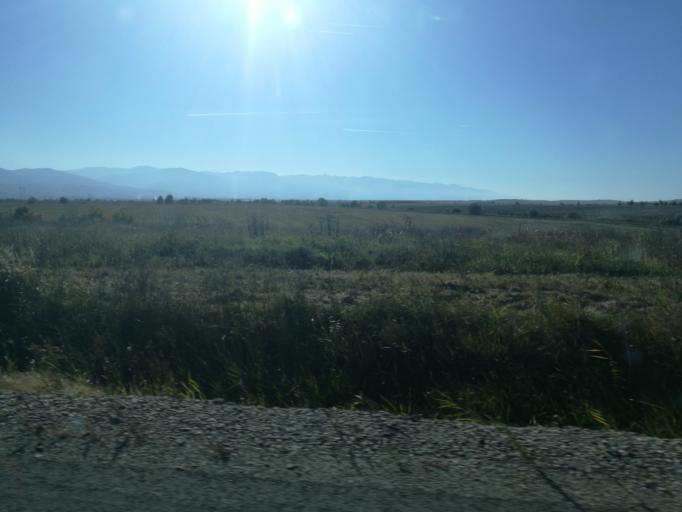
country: RO
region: Brasov
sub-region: Comuna Sinca Veche
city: Sinca Veche
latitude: 45.8048
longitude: 25.1747
